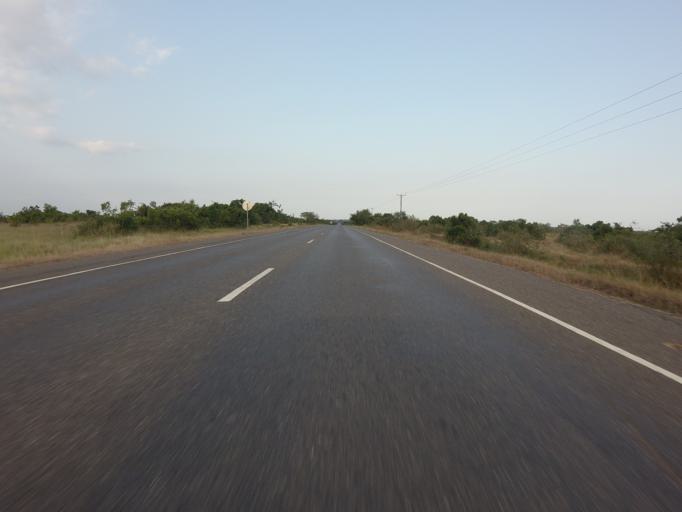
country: GH
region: Volta
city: Anloga
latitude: 6.0797
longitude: 0.5821
